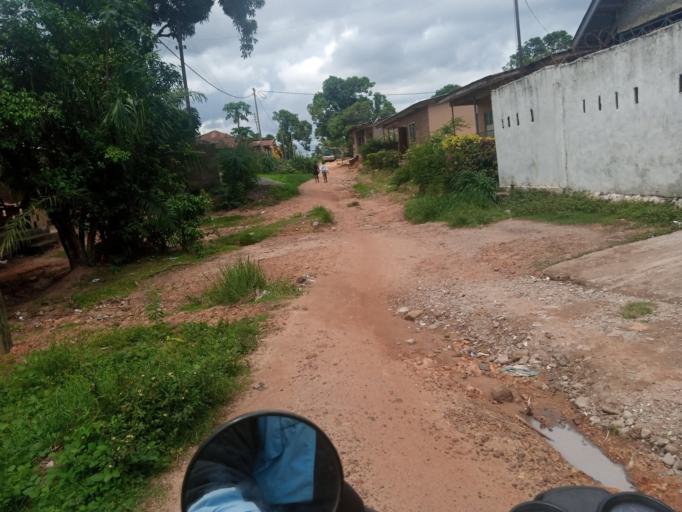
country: SL
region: Southern Province
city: Bo
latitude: 7.9555
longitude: -11.7404
